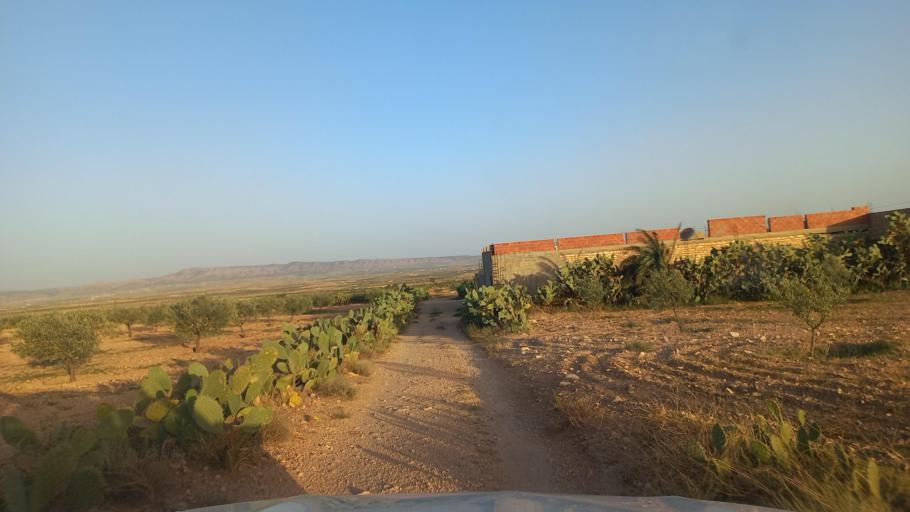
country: TN
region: Al Qasrayn
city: Sbiba
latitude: 35.3729
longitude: 9.0104
